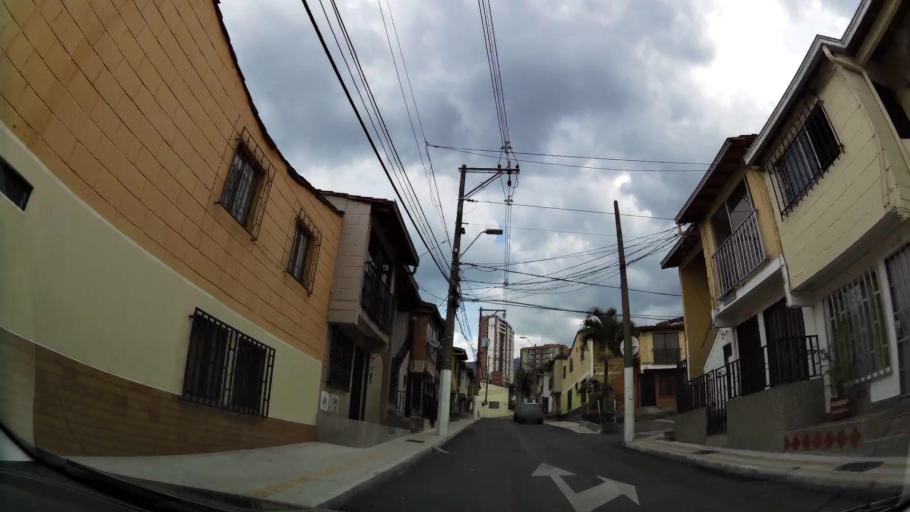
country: CO
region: Antioquia
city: Envigado
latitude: 6.1619
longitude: -75.5930
